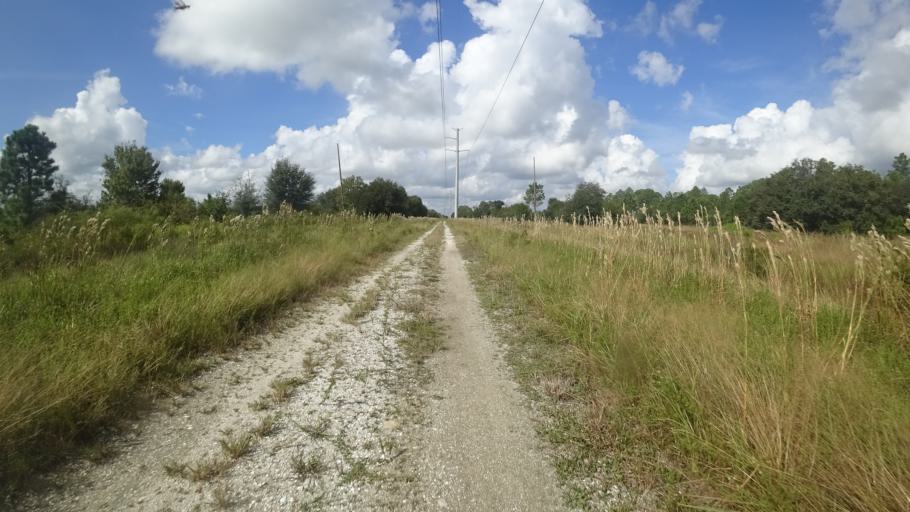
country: US
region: Florida
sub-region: Hillsborough County
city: Wimauma
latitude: 27.5158
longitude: -82.1106
